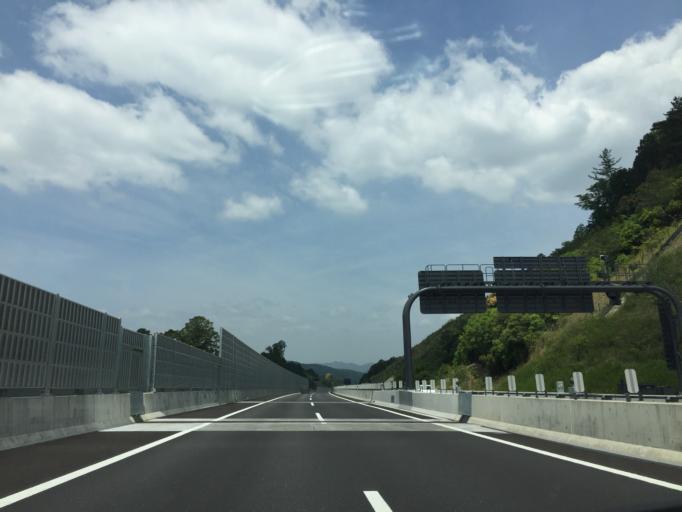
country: JP
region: Aichi
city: Shinshiro
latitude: 34.8960
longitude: 137.6270
